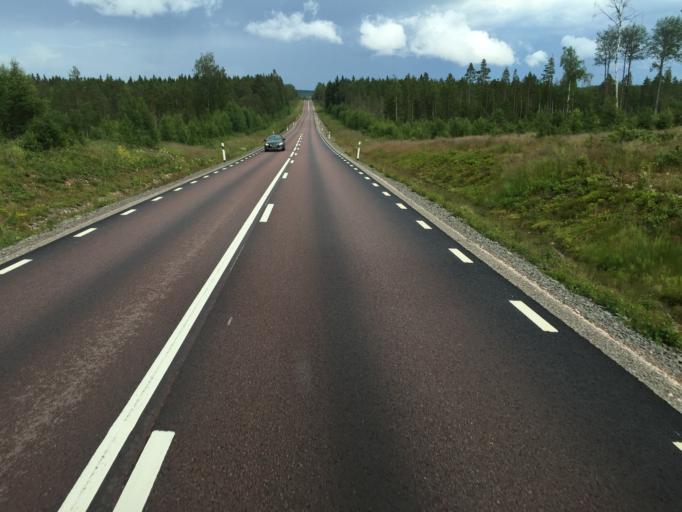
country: SE
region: Dalarna
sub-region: Malung-Saelens kommun
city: Malung
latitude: 60.8246
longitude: 14.0268
